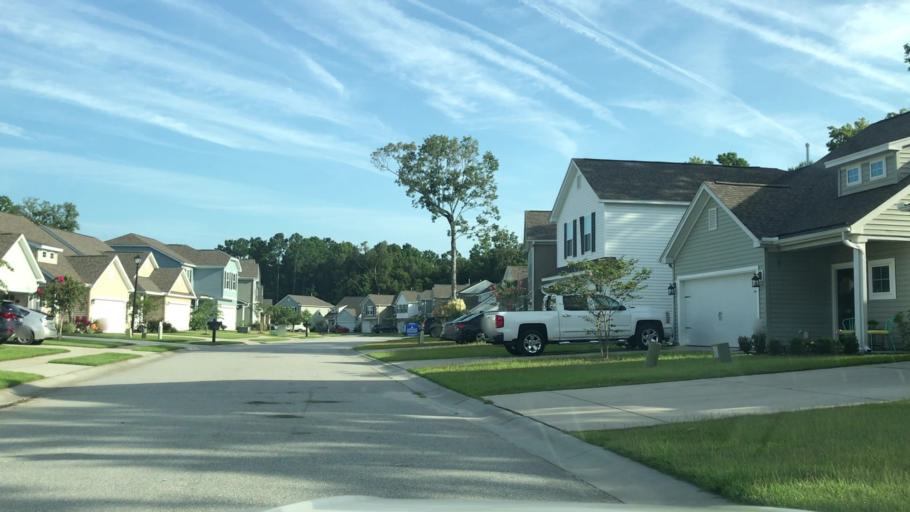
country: US
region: South Carolina
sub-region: Charleston County
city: Isle of Palms
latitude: 32.8914
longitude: -79.7520
